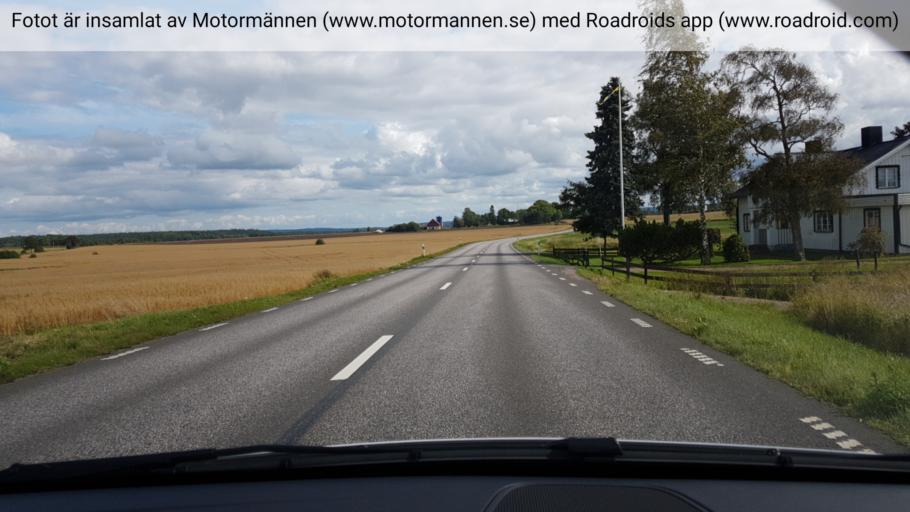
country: SE
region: Joenkoeping
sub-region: Mullsjo Kommun
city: Mullsjoe
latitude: 58.0806
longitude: 13.7805
